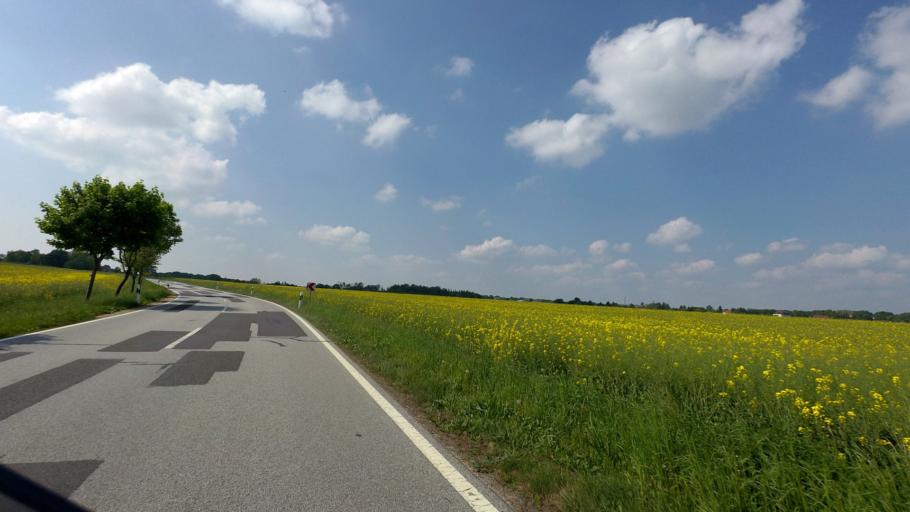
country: DE
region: Saxony
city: Weissenberg
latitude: 51.1867
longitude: 14.6500
